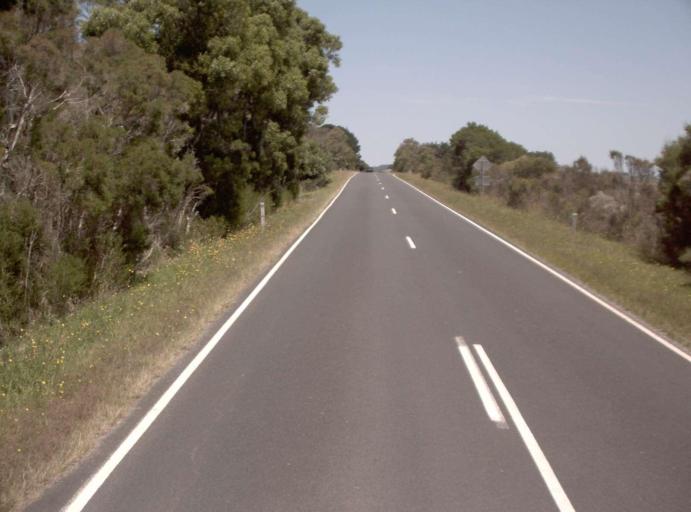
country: AU
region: Victoria
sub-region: Bass Coast
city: North Wonthaggi
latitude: -38.6155
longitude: 145.9670
